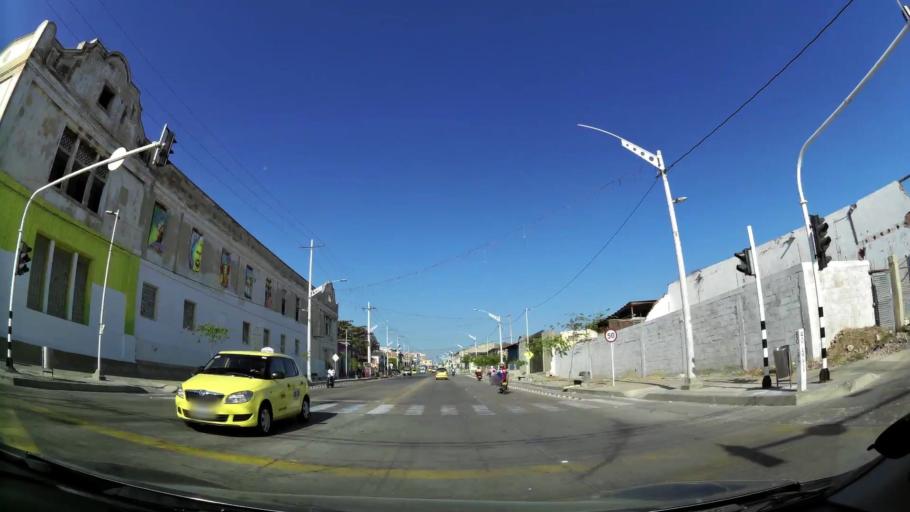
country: CO
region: Atlantico
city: Barranquilla
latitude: 10.9888
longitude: -74.7805
